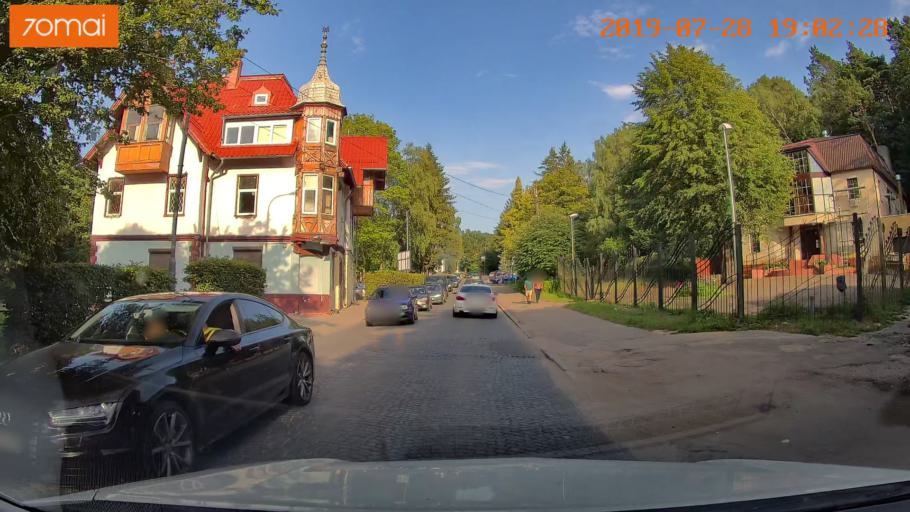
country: RU
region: Kaliningrad
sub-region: Gorod Svetlogorsk
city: Svetlogorsk
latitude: 54.9382
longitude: 20.1605
